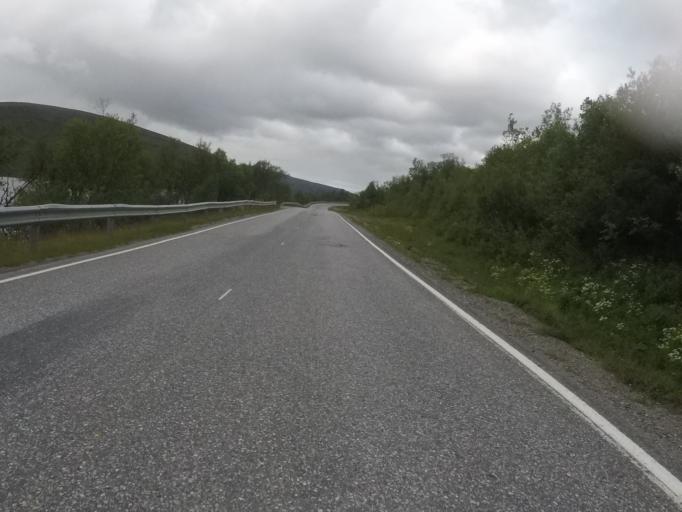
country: NO
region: Finnmark Fylke
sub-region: Alta
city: Alta
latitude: 69.6743
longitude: 23.4322
